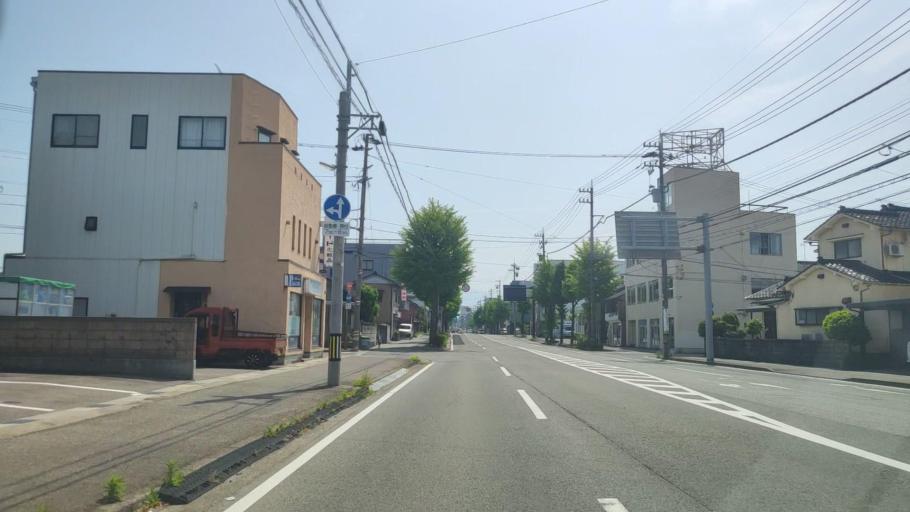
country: JP
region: Toyama
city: Toyama-shi
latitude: 36.6969
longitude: 137.2213
